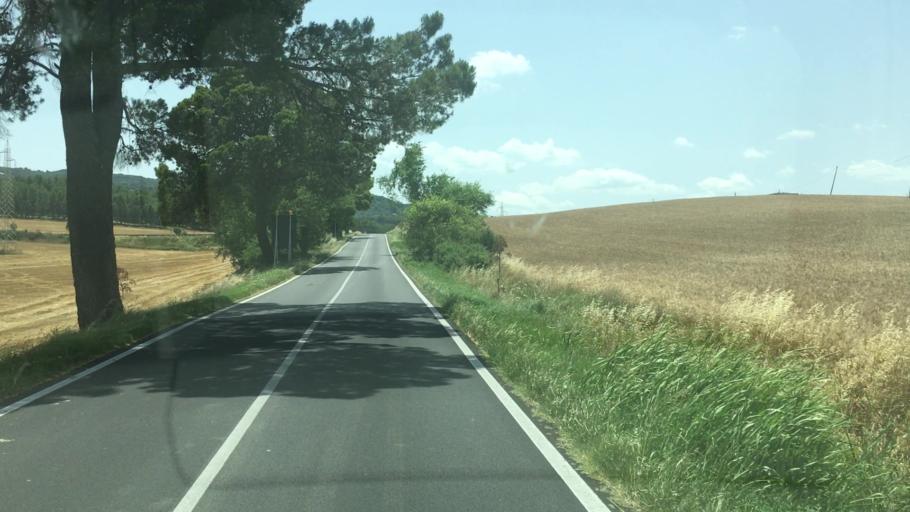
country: IT
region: Basilicate
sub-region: Provincia di Matera
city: La Martella
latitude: 40.6700
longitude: 16.4895
